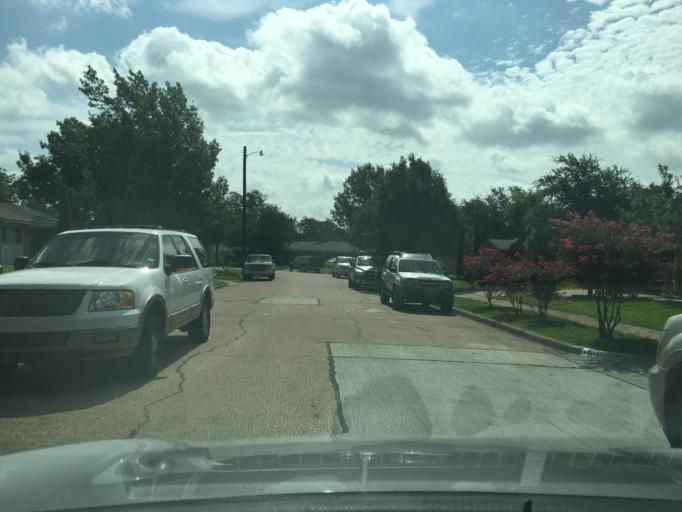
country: US
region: Texas
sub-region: Dallas County
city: Richardson
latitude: 32.9211
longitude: -96.6977
